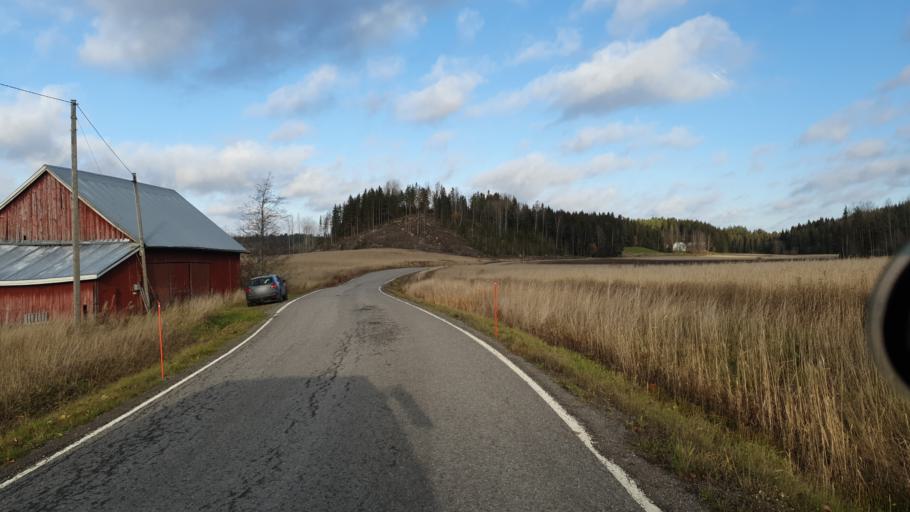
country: FI
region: Uusimaa
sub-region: Helsinki
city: Siuntio
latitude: 60.2538
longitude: 24.2997
